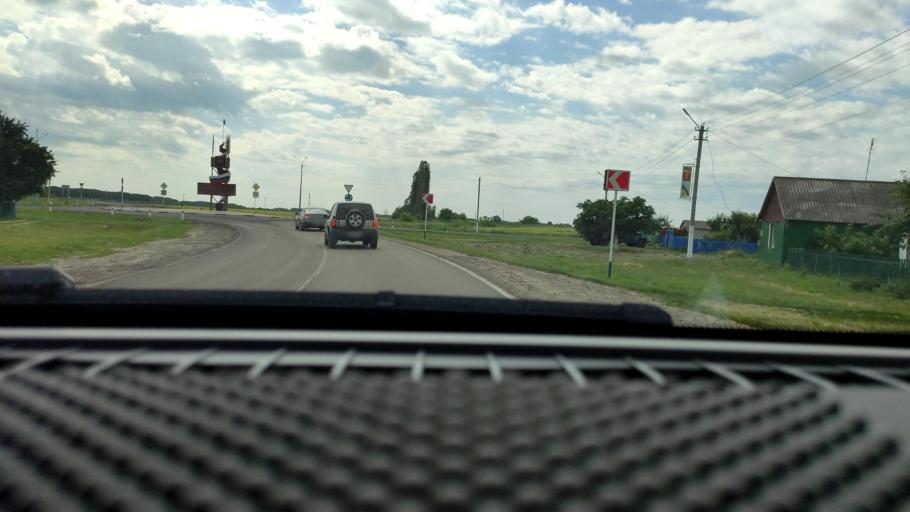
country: RU
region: Voronezj
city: Panino
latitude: 51.6447
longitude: 40.1184
